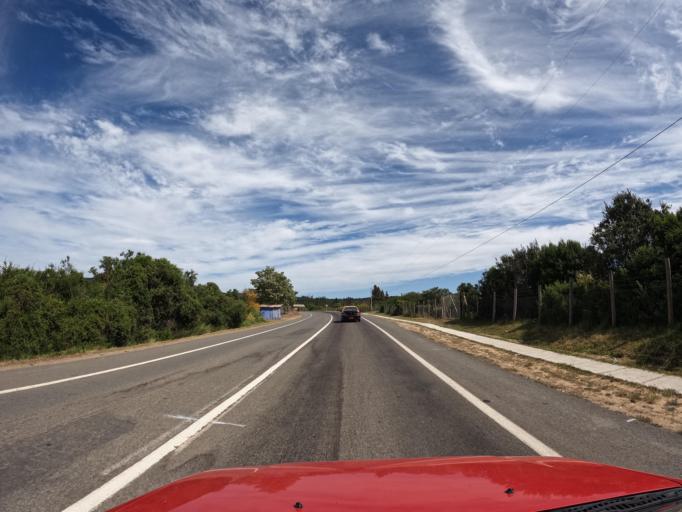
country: CL
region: Maule
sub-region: Provincia de Talca
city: Talca
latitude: -35.1247
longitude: -71.9576
